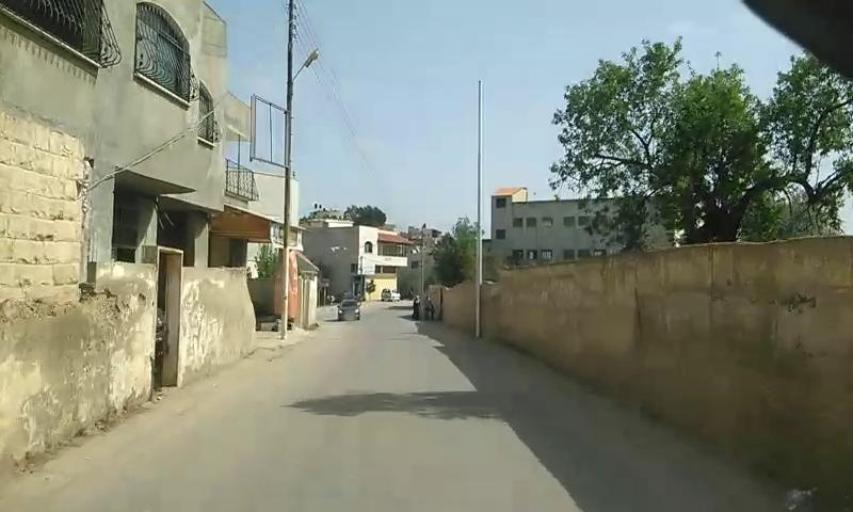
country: PS
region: West Bank
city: Birqin
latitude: 32.4514
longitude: 35.2627
